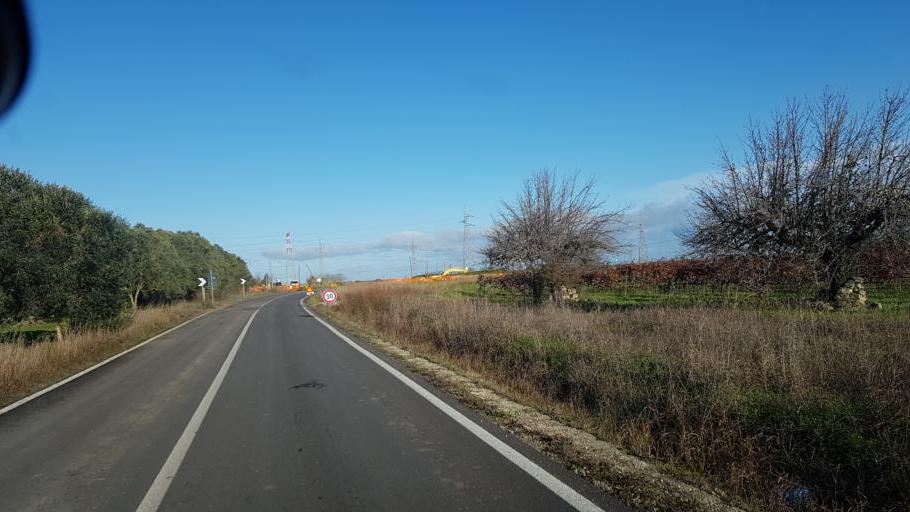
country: IT
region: Apulia
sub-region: Provincia di Brindisi
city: Tuturano
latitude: 40.5512
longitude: 17.9470
